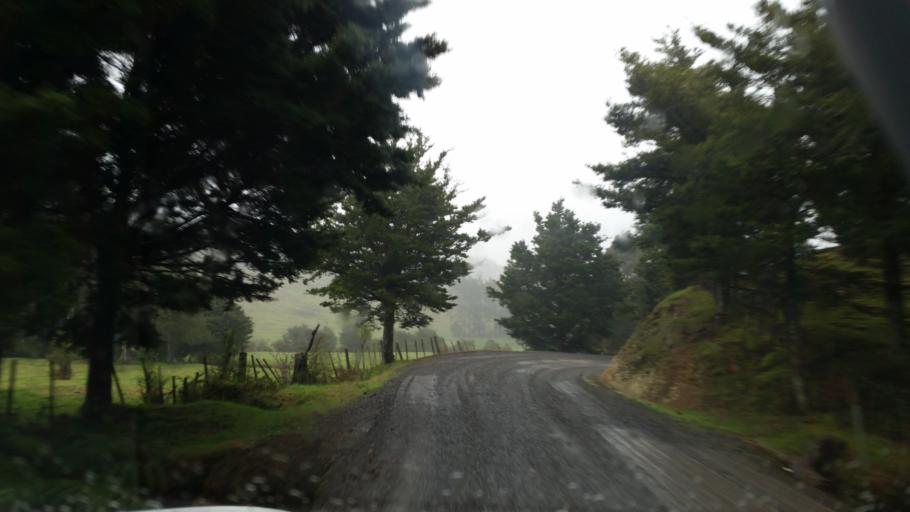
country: NZ
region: Northland
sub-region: Whangarei
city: Ngunguru
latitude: -35.4971
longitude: 174.4277
